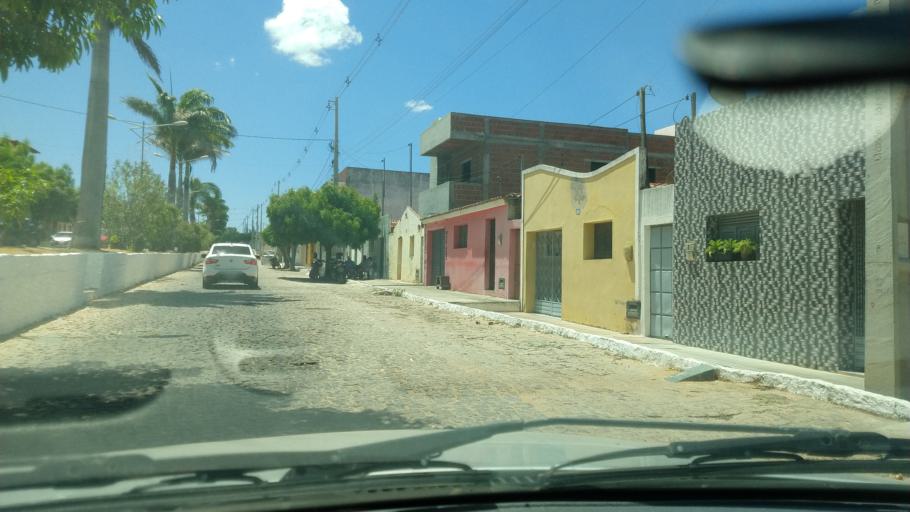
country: BR
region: Rio Grande do Norte
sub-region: Cerro Cora
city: Cerro Cora
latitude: -6.0481
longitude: -36.3504
